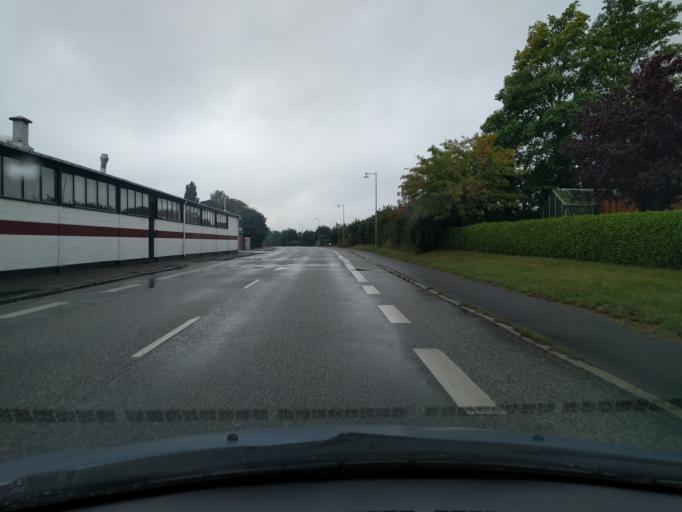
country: DK
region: Zealand
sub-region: Guldborgsund Kommune
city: Stubbekobing
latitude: 54.8885
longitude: 12.0305
